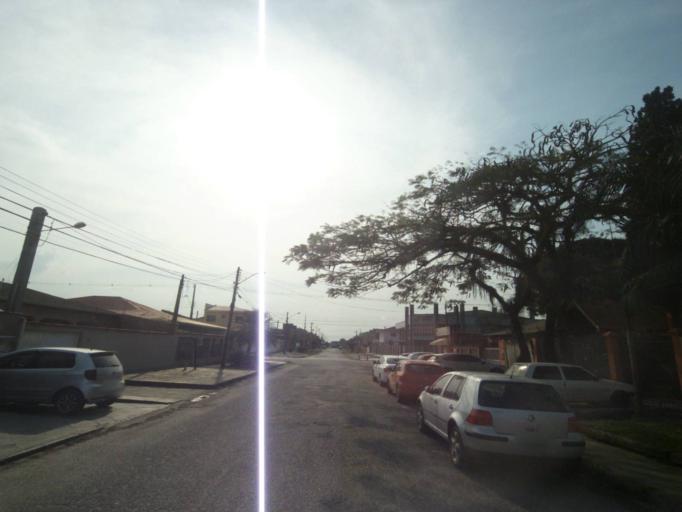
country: BR
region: Parana
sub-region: Paranagua
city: Paranagua
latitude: -25.5223
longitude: -48.5299
